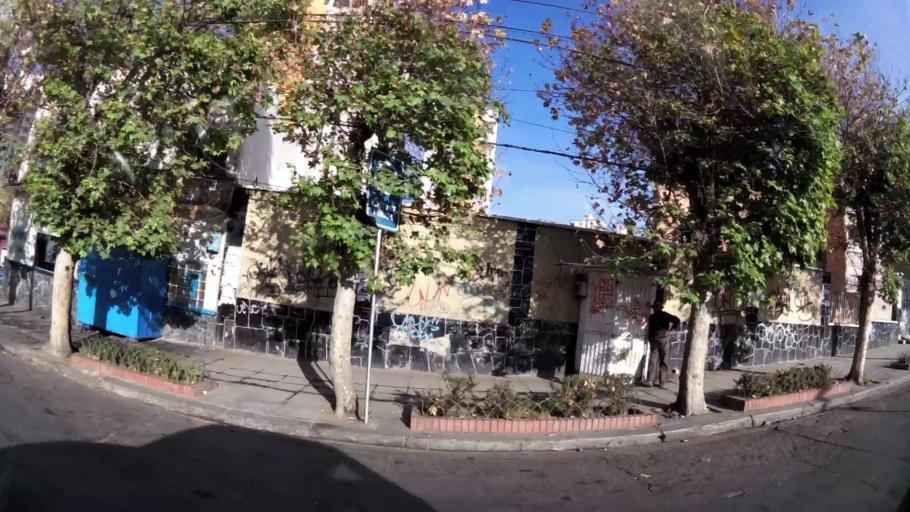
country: BO
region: La Paz
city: La Paz
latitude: -16.5012
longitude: -68.1211
